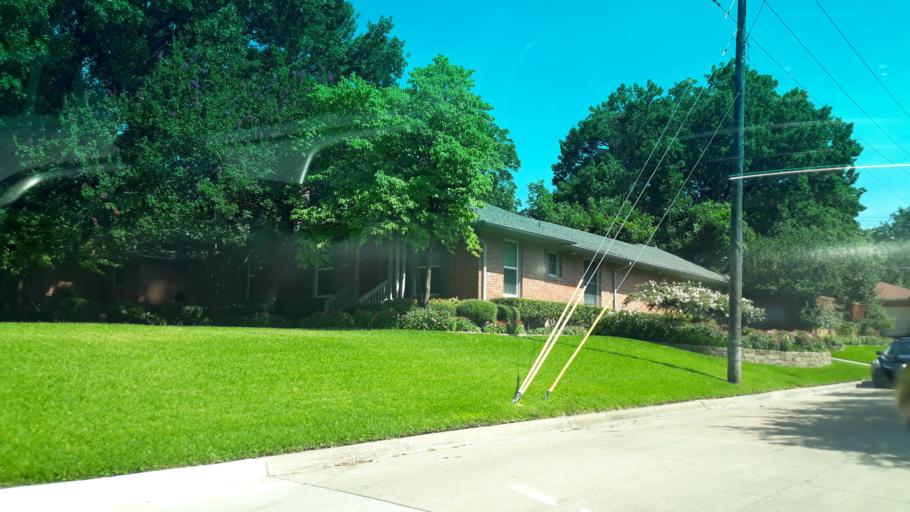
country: US
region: Texas
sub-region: Dallas County
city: Highland Park
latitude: 32.8219
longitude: -96.7428
